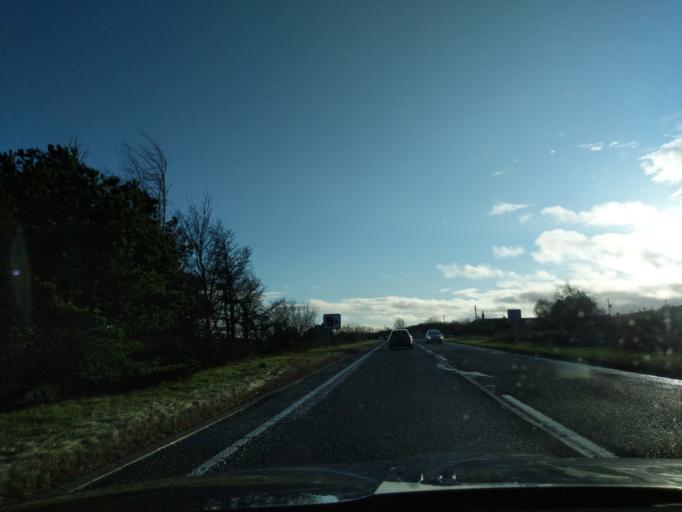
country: GB
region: England
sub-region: Northumberland
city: Belford
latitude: 55.5462
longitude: -1.7859
